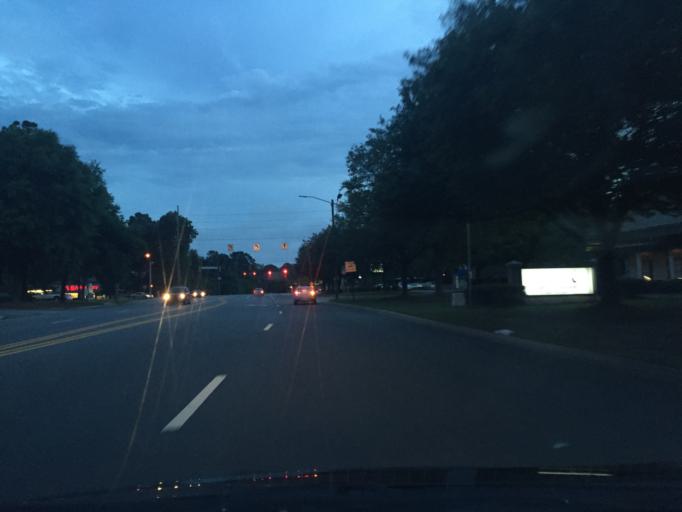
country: US
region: Georgia
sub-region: Chatham County
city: Isle of Hope
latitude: 31.9975
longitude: -81.1148
